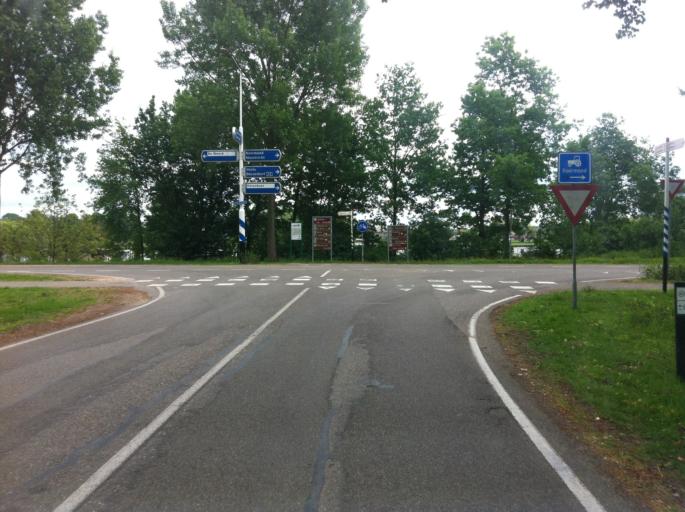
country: NL
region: Limburg
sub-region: Gemeente Roermond
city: Roermond
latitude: 51.2010
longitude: 5.9762
